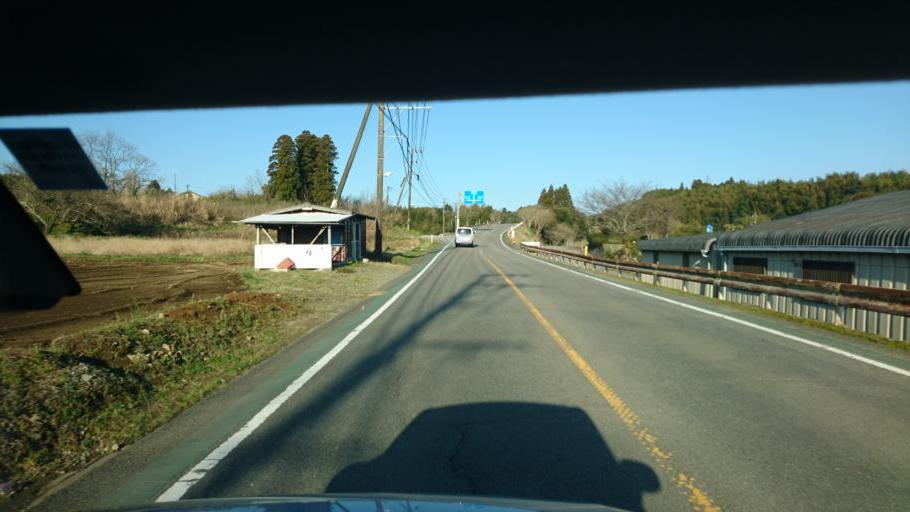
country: JP
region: Miyazaki
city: Miyazaki-shi
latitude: 31.8574
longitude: 131.3717
